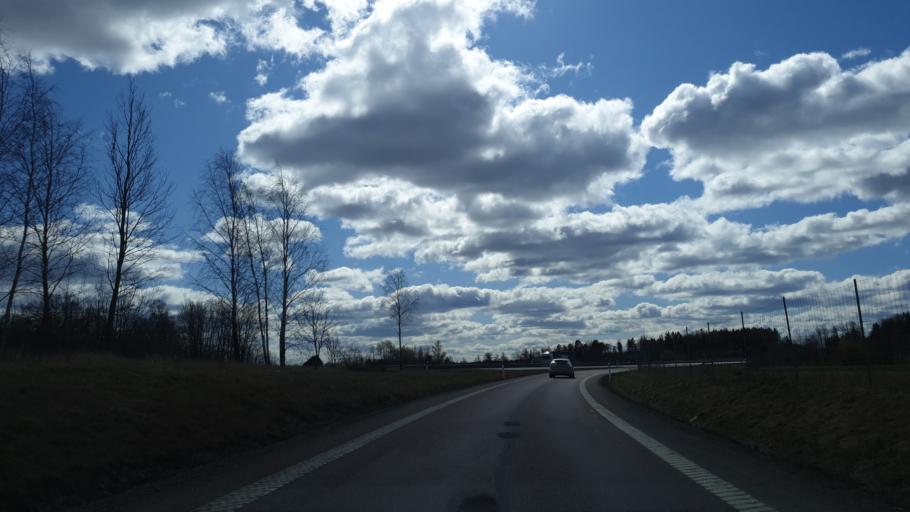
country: SE
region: Vaestmanland
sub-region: Kopings Kommun
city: Koping
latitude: 59.4998
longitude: 15.9303
